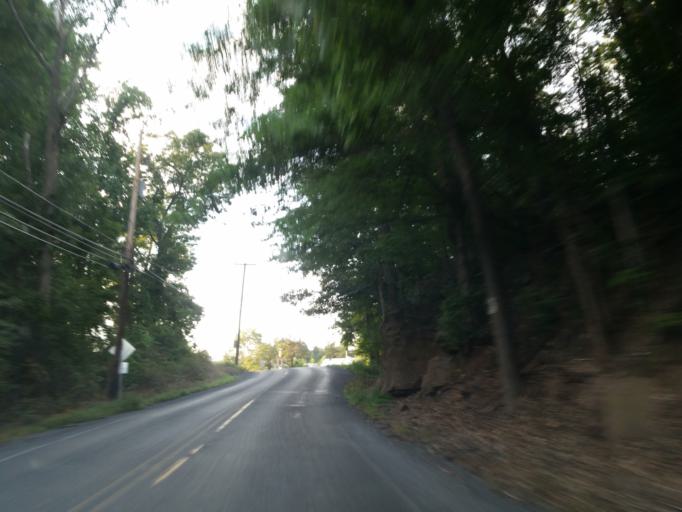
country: US
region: Pennsylvania
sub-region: Berks County
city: Alleghenyville
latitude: 40.2417
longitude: -75.9952
